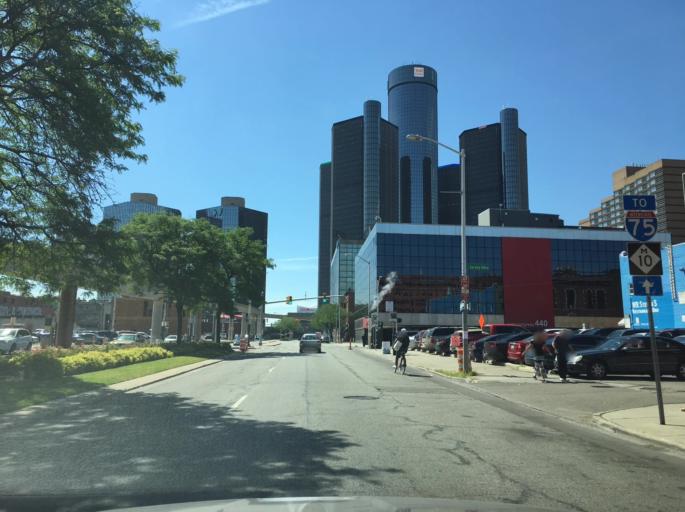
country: US
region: Michigan
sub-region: Wayne County
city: Detroit
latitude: 42.3330
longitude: -83.0412
